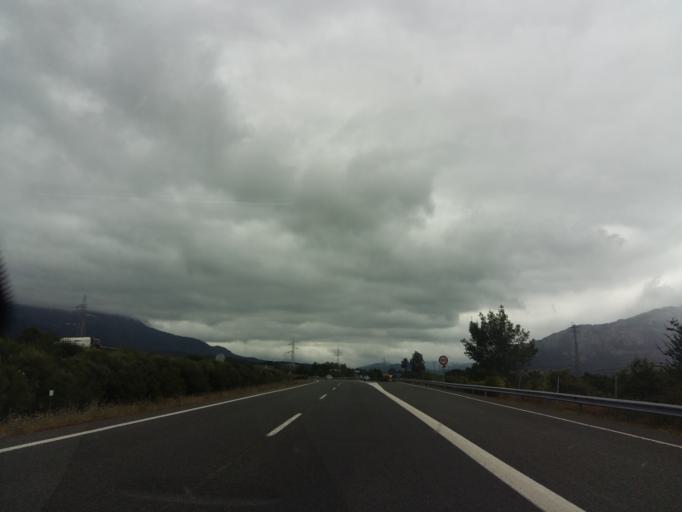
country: ES
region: Navarre
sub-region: Provincia de Navarra
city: Iraneta
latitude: 42.9157
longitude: -1.9140
